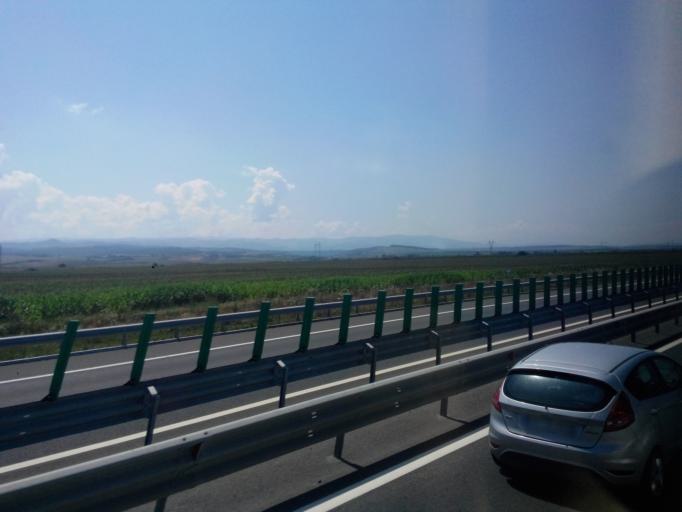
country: RO
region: Alba
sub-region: Oras Cugir
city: Vinerea
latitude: 45.9052
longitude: 23.3066
